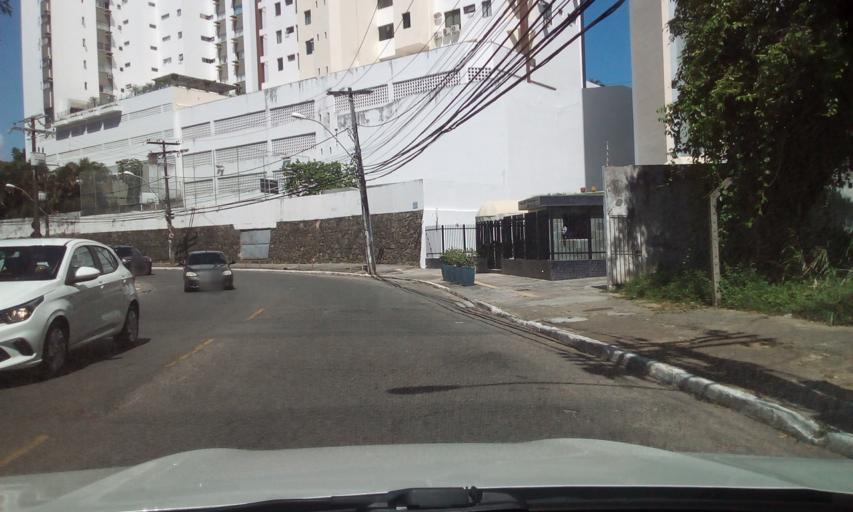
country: BR
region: Bahia
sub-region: Salvador
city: Salvador
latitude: -12.9914
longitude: -38.4669
